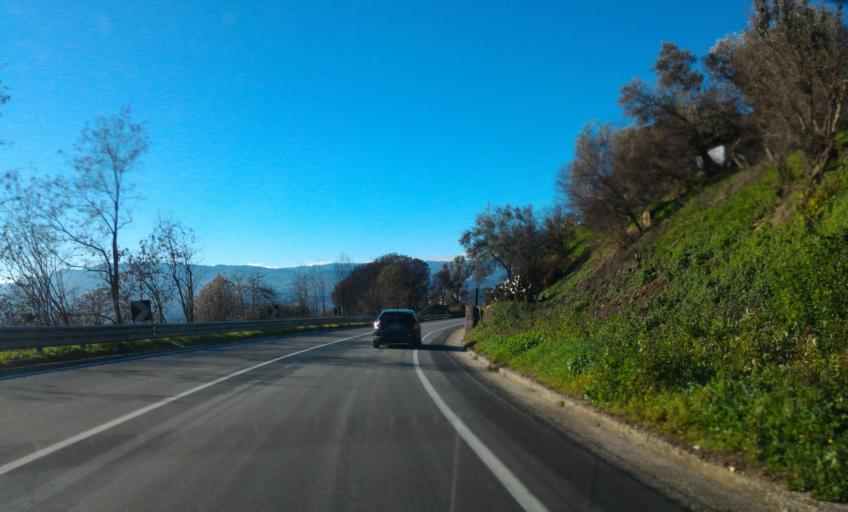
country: IT
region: Calabria
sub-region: Provincia di Cosenza
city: Rovito
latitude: 39.3004
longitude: 16.3134
